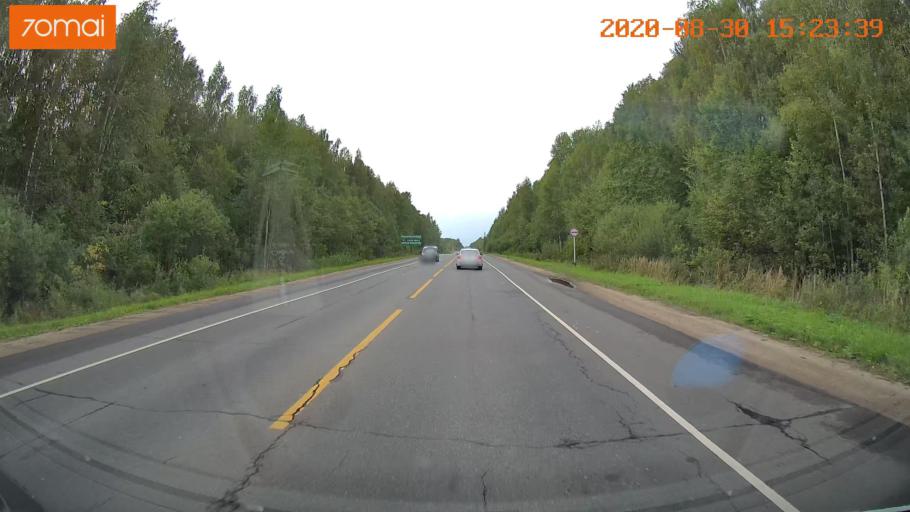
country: RU
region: Ivanovo
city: Rodniki
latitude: 57.0881
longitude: 41.6995
